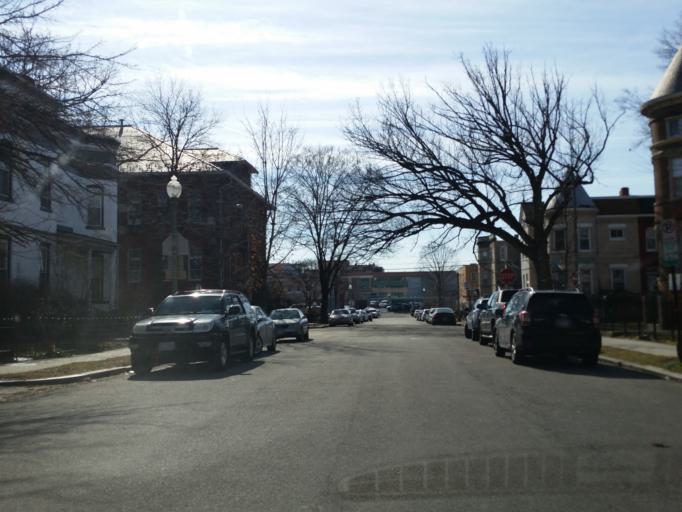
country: US
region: Washington, D.C.
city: Washington, D.C.
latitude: 38.9123
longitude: -77.0065
